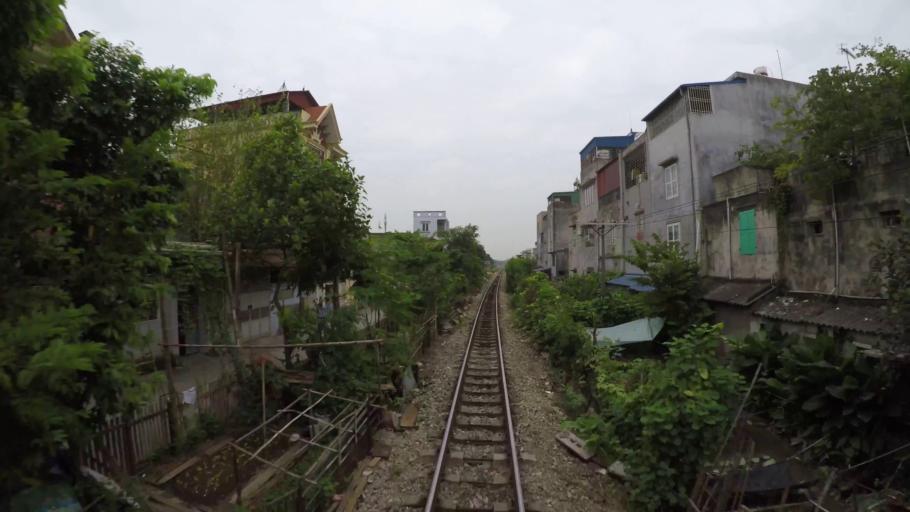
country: VN
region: Hai Phong
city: An Duong
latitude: 20.8855
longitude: 106.6022
